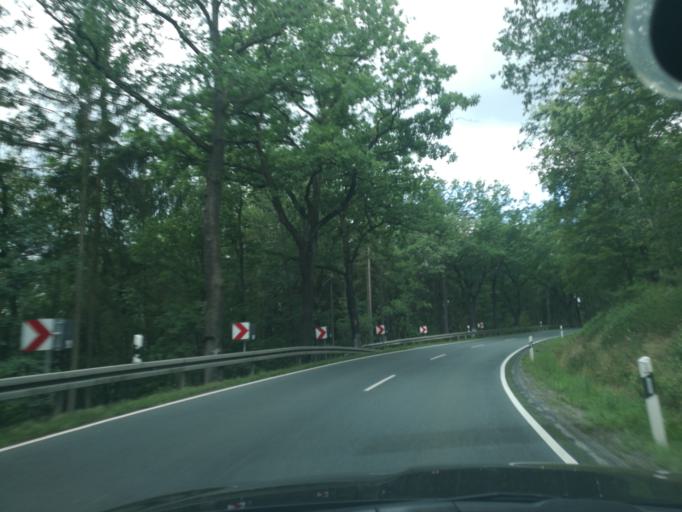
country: DE
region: Saxony
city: Oelsnitz
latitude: 50.3864
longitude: 12.1953
